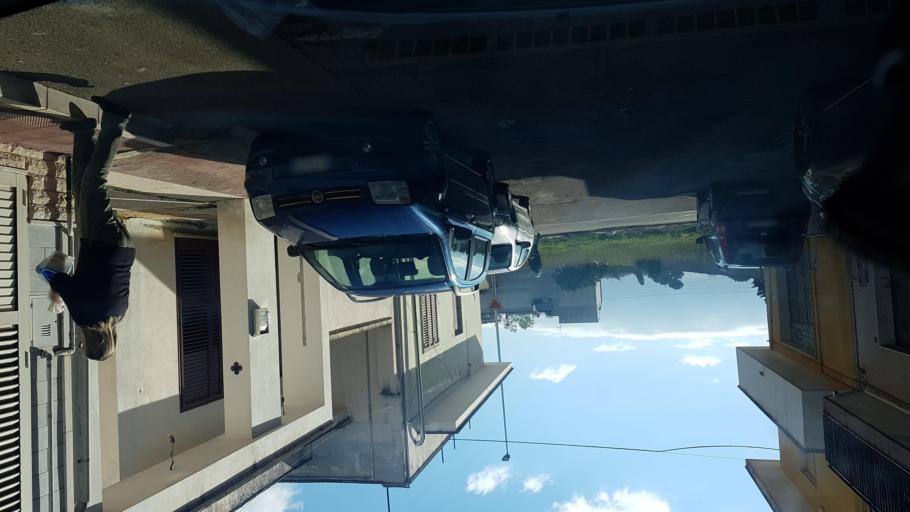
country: IT
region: Apulia
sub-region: Provincia di Brindisi
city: San Pietro Vernotico
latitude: 40.4865
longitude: 17.9897
